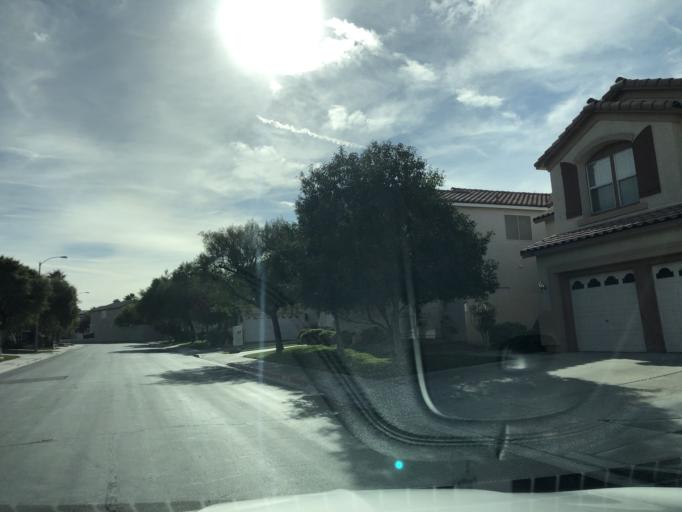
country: US
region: Nevada
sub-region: Clark County
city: Whitney
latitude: 36.0161
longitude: -115.0892
